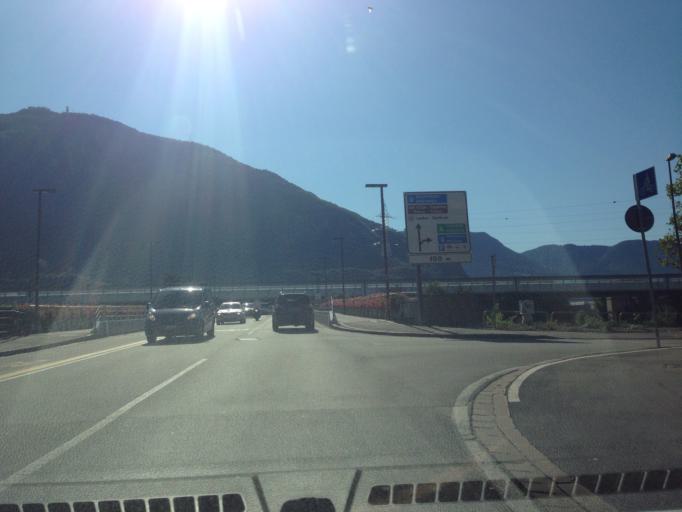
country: IT
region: Trentino-Alto Adige
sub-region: Bolzano
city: Bolzano
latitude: 46.4824
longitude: 11.3223
